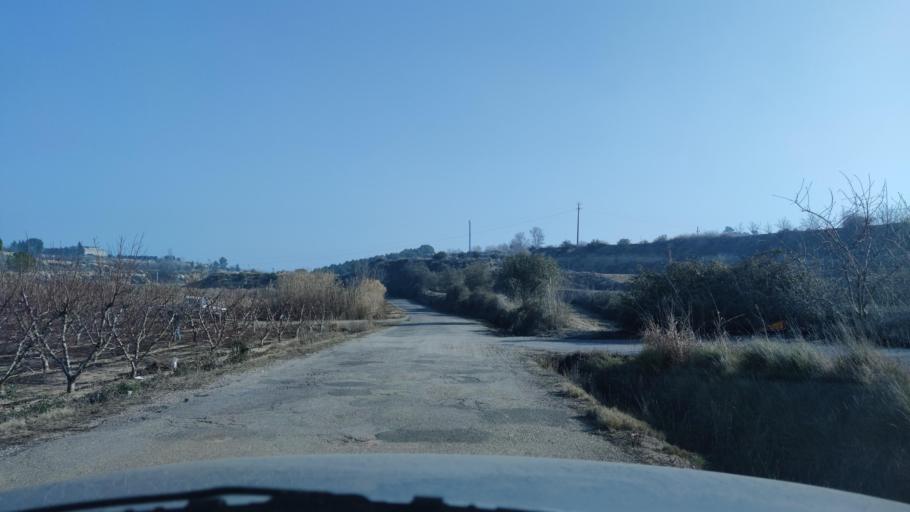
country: ES
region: Catalonia
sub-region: Provincia de Lleida
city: Seros
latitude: 41.4650
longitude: 0.3984
